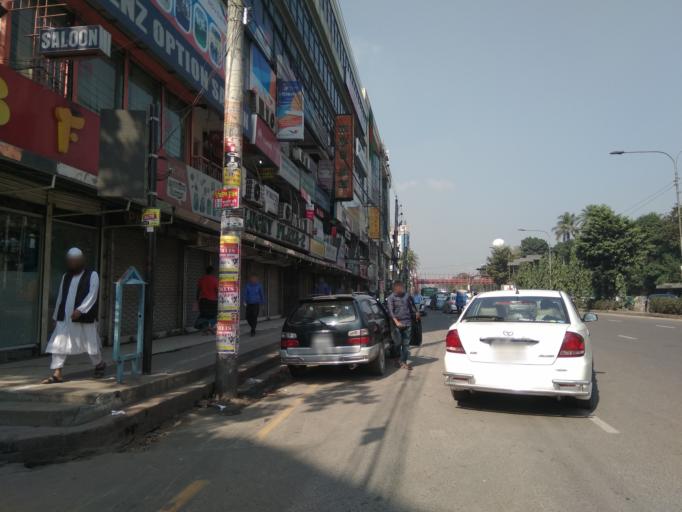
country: BD
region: Dhaka
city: Azimpur
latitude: 23.7555
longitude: 90.3756
